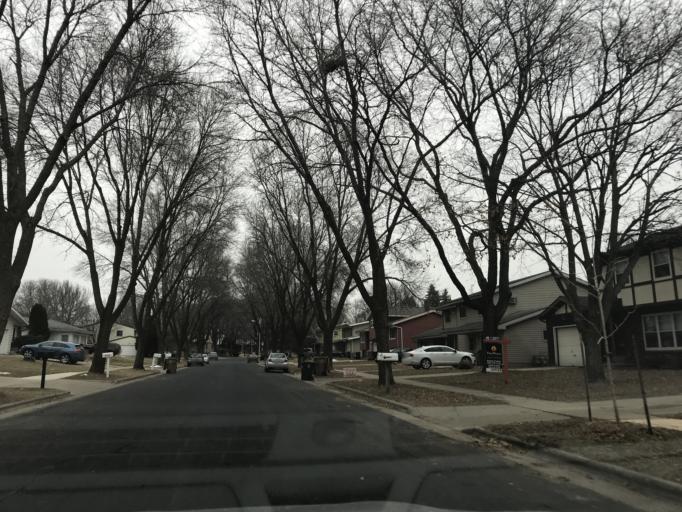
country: US
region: Wisconsin
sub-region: Dane County
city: Monona
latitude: 43.1031
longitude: -89.3041
